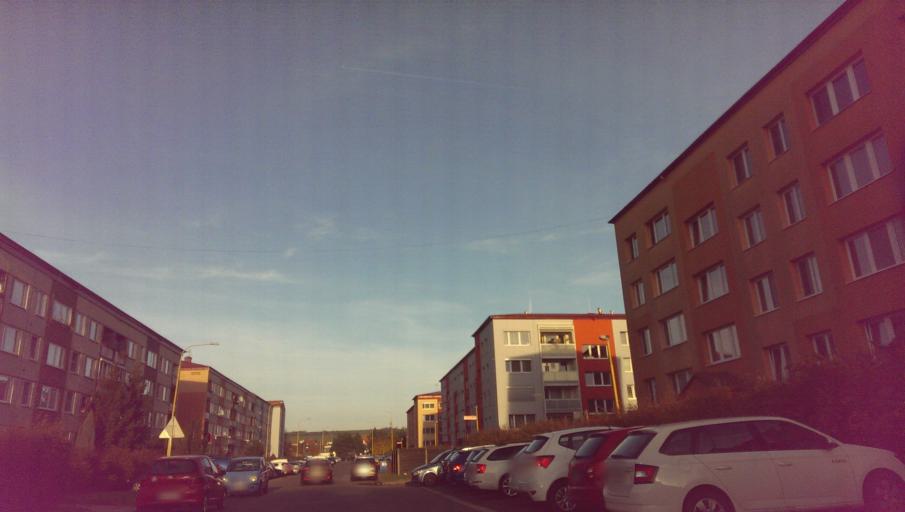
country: CZ
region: Zlin
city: Kunovice
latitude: 49.0580
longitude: 17.4815
